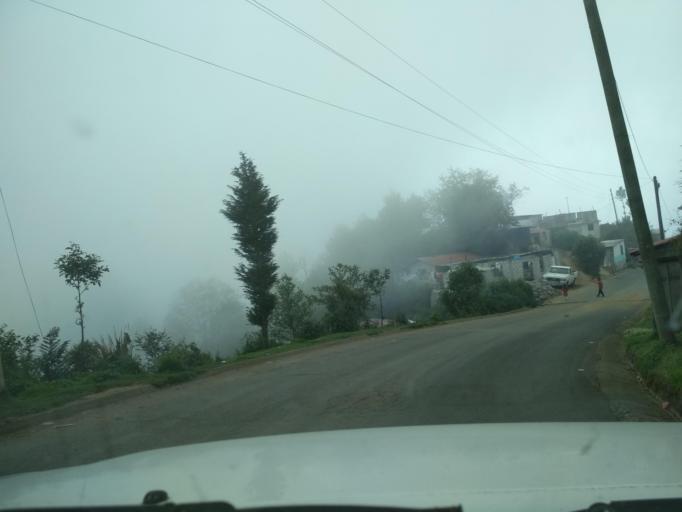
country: MX
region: Veracruz
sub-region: La Perla
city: Chilapa
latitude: 18.9740
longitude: -97.1739
